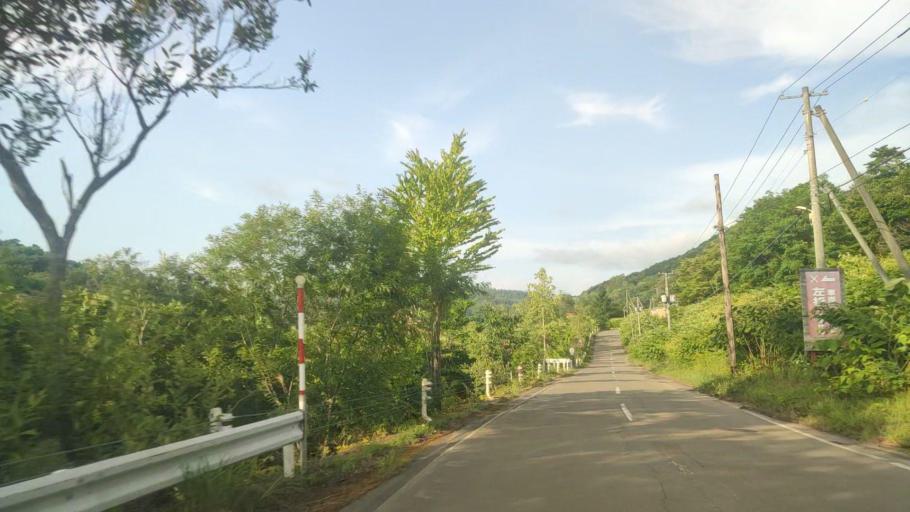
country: JP
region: Hokkaido
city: Iwamizawa
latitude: 43.0625
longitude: 141.9825
